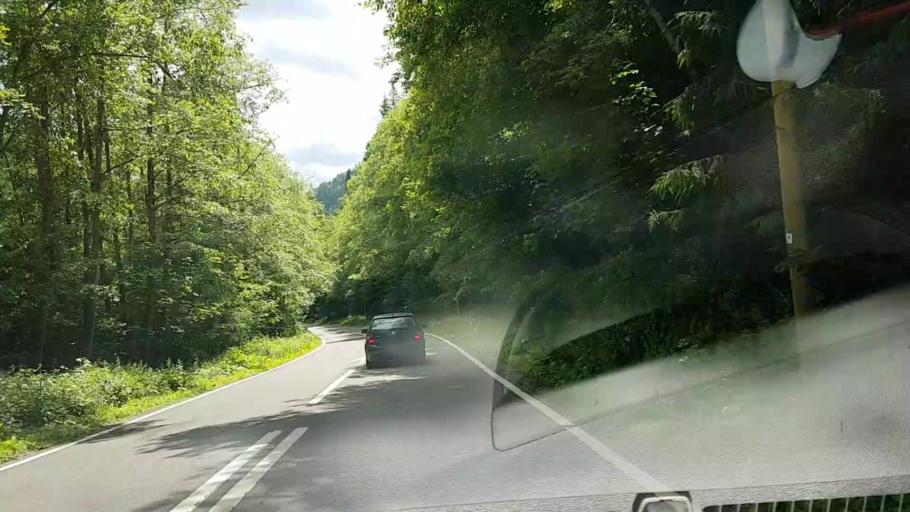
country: RO
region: Suceava
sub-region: Comuna Crucea
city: Crucea
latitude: 47.2903
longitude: 25.6331
